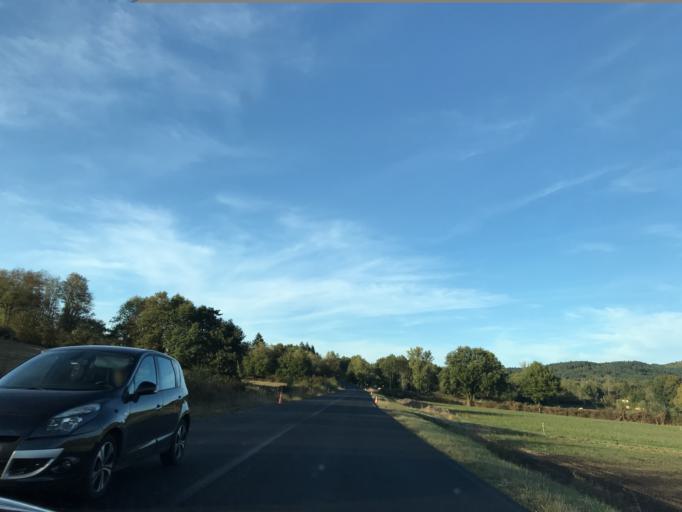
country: FR
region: Auvergne
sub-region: Departement du Puy-de-Dome
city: Paslieres
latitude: 45.8963
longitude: 3.5185
